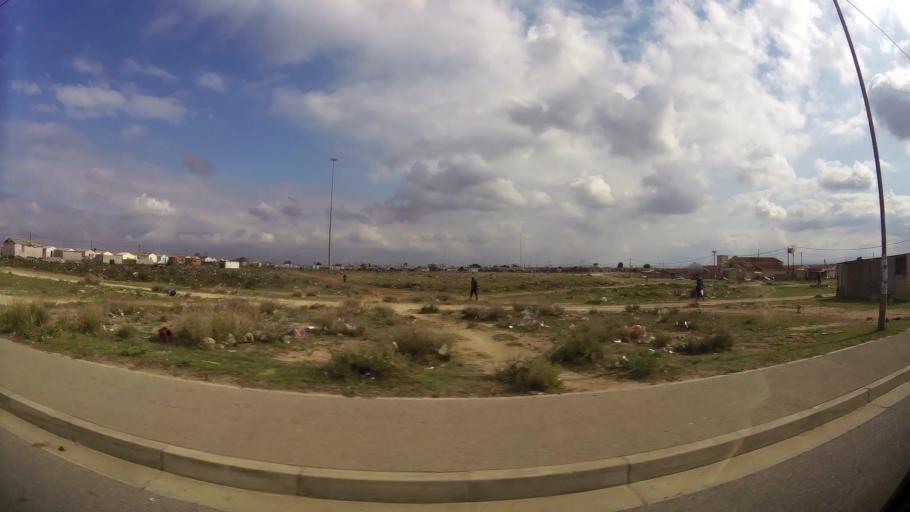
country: ZA
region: Eastern Cape
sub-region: Nelson Mandela Bay Metropolitan Municipality
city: Port Elizabeth
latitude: -33.7910
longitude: 25.5803
